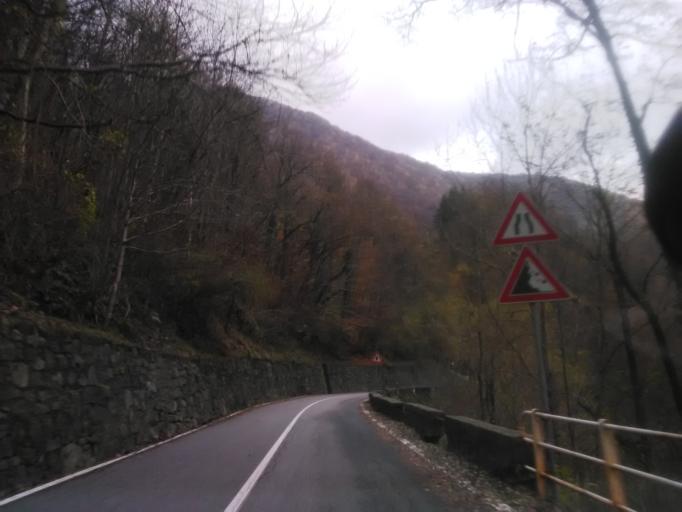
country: IT
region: Piedmont
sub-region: Provincia di Vercelli
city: Sabbia
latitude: 45.8458
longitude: 8.2456
